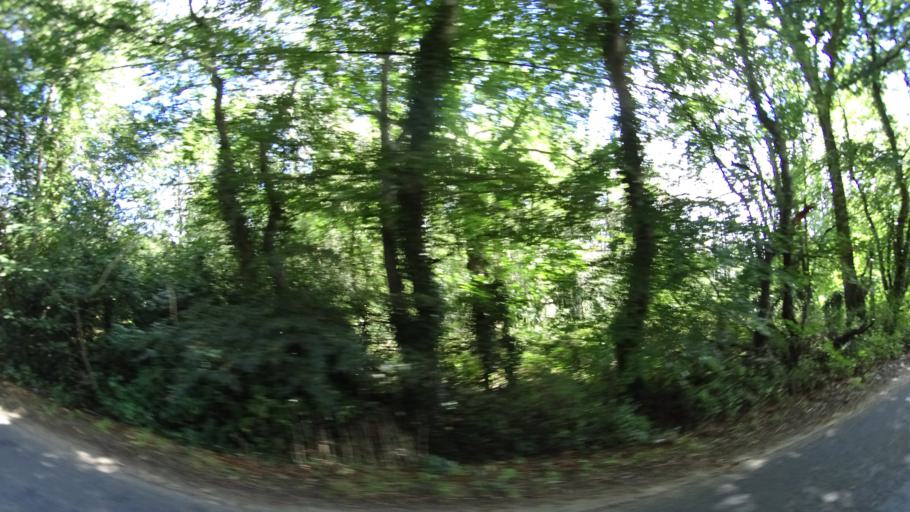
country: GB
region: England
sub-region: Hampshire
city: Romsey
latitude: 51.0058
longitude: -1.4724
